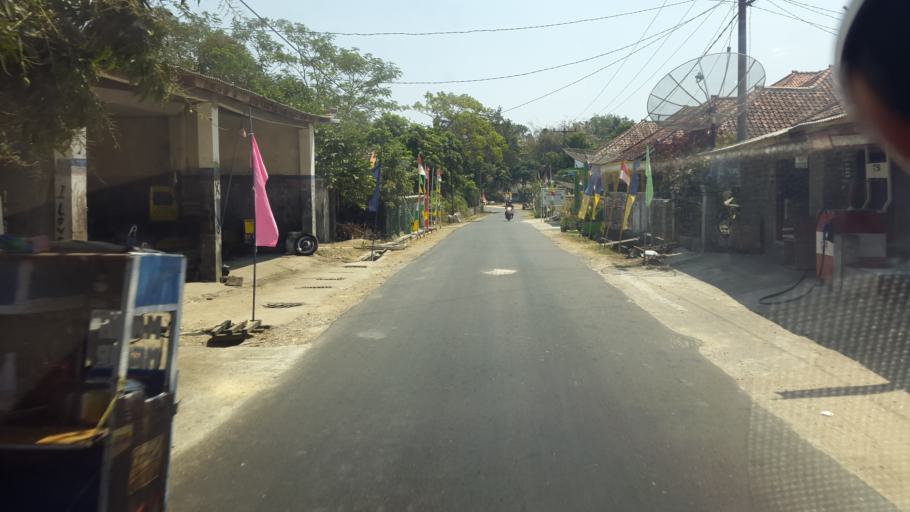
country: ID
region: West Java
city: Citeureup
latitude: -7.3307
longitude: 106.5188
